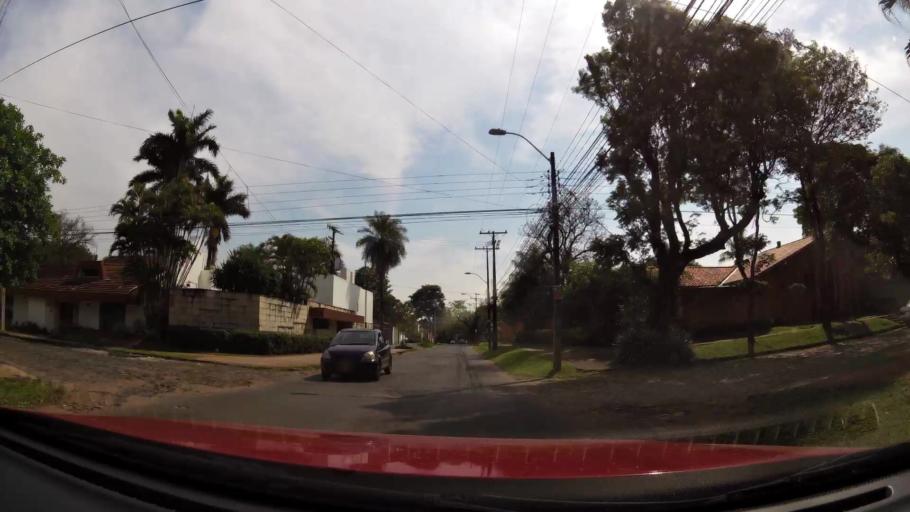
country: PY
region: Asuncion
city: Asuncion
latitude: -25.2686
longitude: -57.5627
